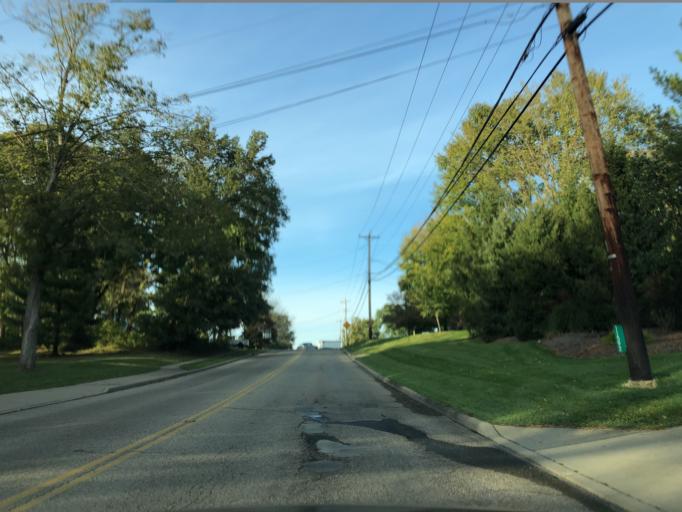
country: US
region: Ohio
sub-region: Hamilton County
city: Loveland
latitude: 39.2727
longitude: -84.2735
